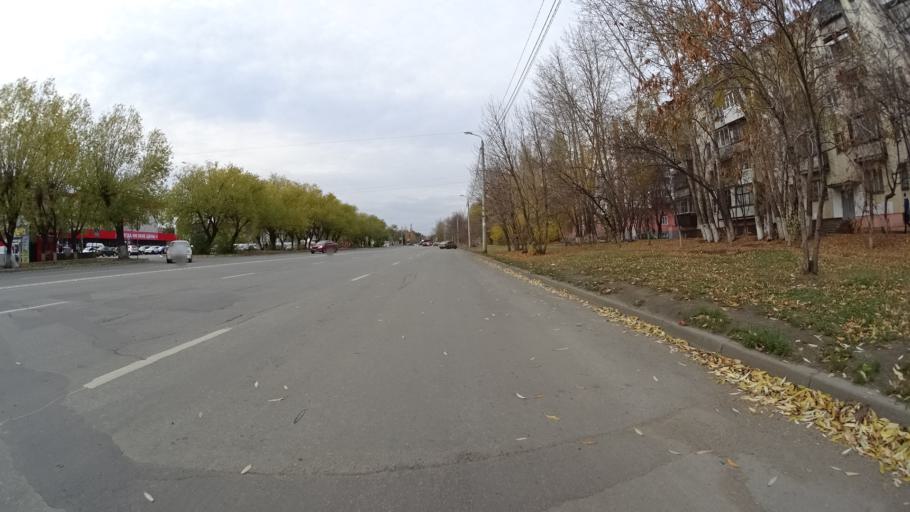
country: RU
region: Chelyabinsk
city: Roshchino
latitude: 55.1921
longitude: 61.3040
